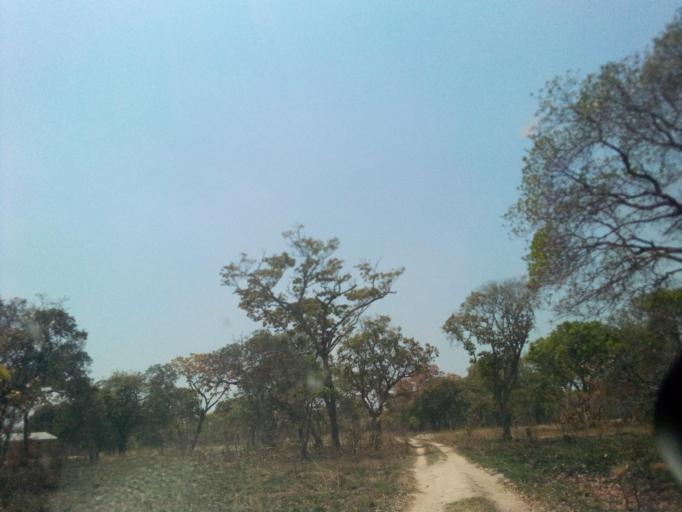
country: ZM
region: Copperbelt
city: Kataba
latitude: -12.2391
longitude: 30.4041
